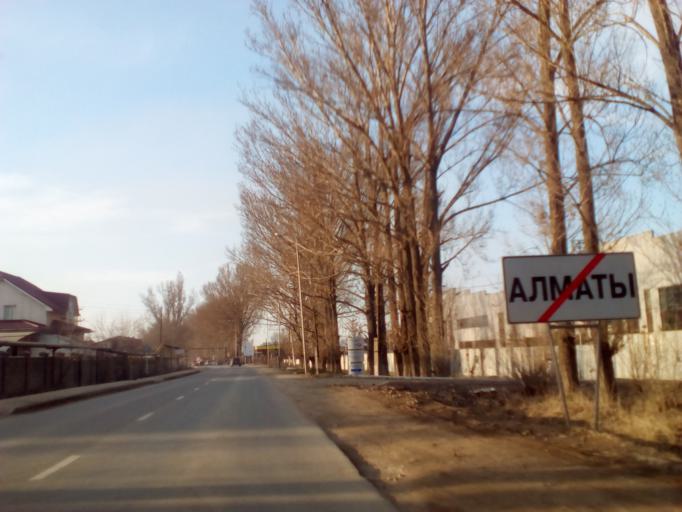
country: KZ
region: Almaty Oblysy
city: Burunday
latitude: 43.2513
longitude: 76.7837
